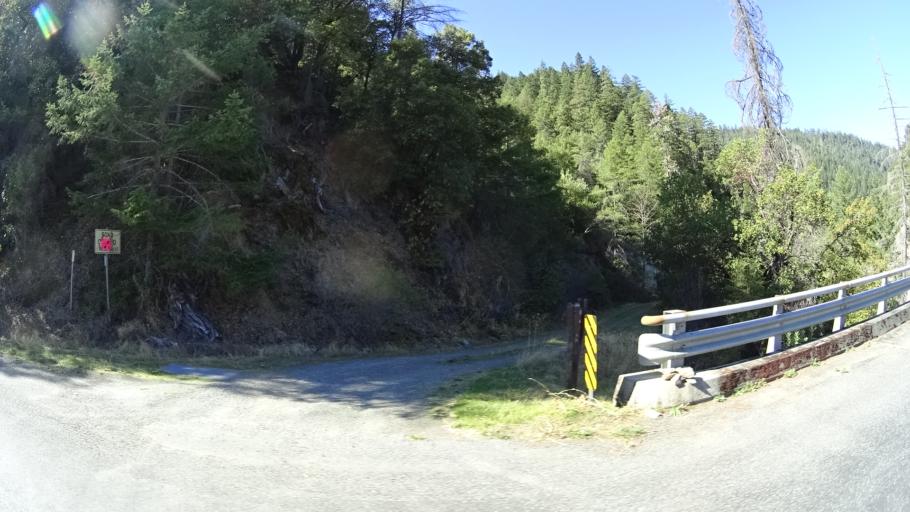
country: US
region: California
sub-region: Siskiyou County
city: Happy Camp
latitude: 41.3767
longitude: -123.4947
